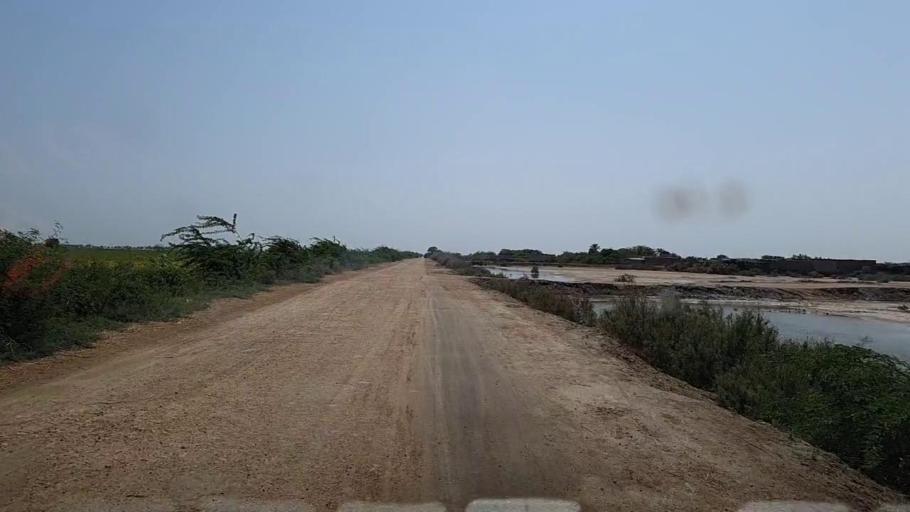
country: PK
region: Sindh
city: Mirpur Batoro
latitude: 24.6321
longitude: 68.4522
